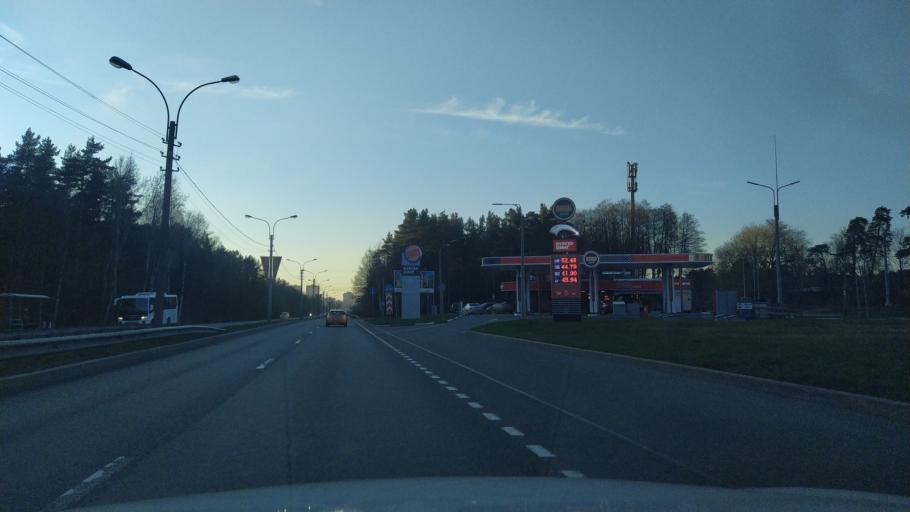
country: RU
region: St.-Petersburg
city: Tarkhovka
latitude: 60.0705
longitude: 29.9697
